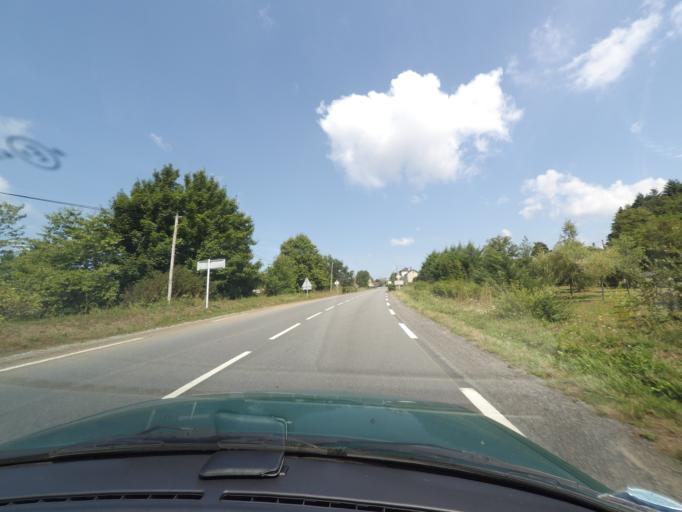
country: FR
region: Limousin
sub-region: Departement de la Haute-Vienne
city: Linards
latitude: 45.7668
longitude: 1.5400
